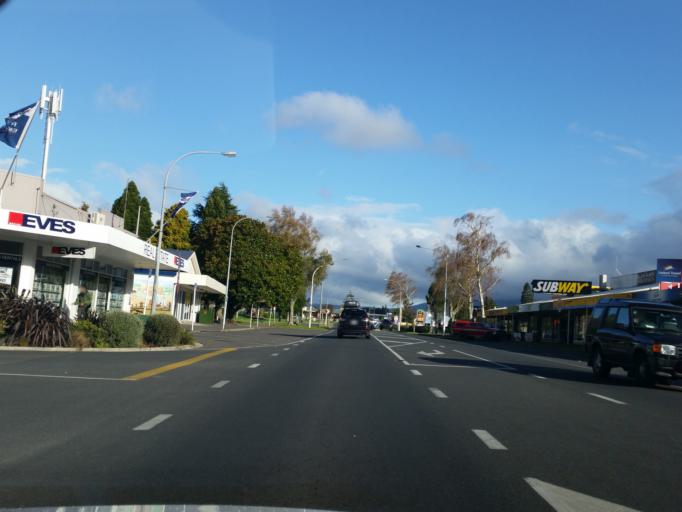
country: NZ
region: Bay of Plenty
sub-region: Western Bay of Plenty District
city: Katikati
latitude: -37.5545
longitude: 175.9171
